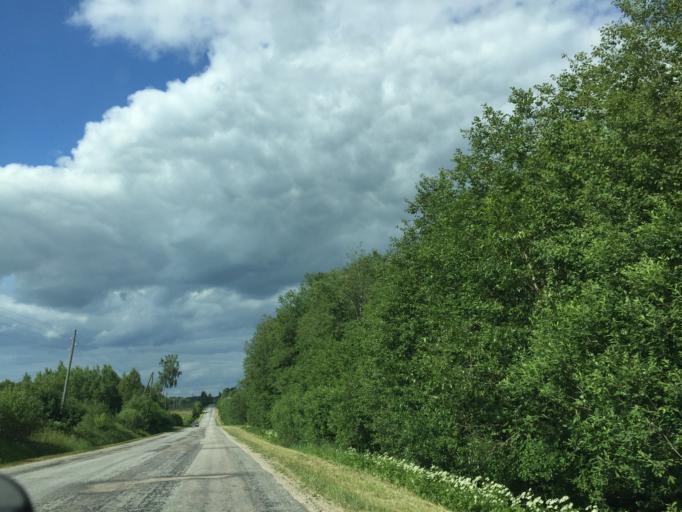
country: LV
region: Skriveri
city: Skriveri
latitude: 56.8127
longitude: 25.1152
